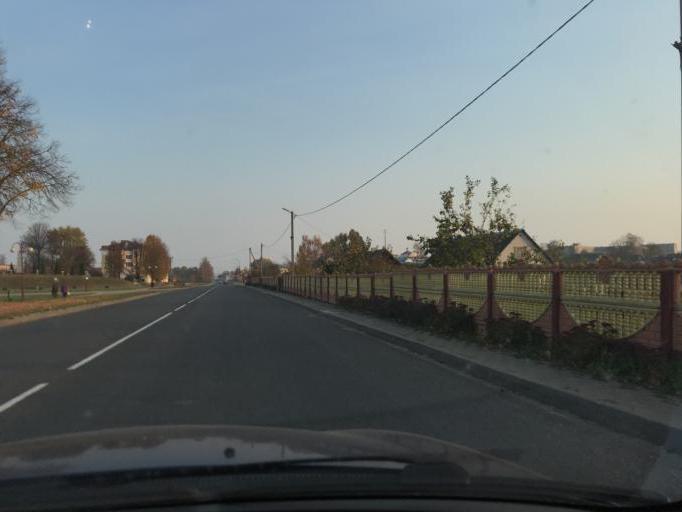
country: BY
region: Grodnenskaya
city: Karelichy
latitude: 53.5761
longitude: 26.1317
